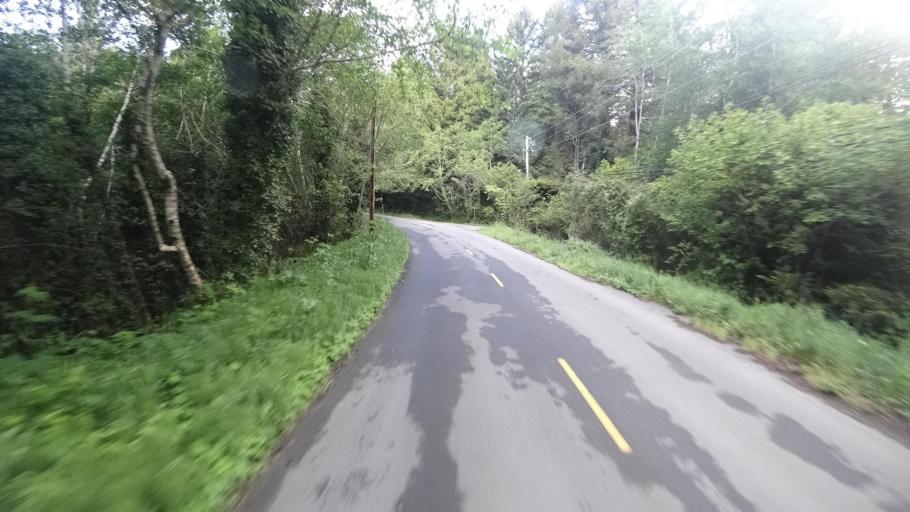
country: US
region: California
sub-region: Humboldt County
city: Westhaven-Moonstone
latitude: 41.0598
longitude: -124.1267
